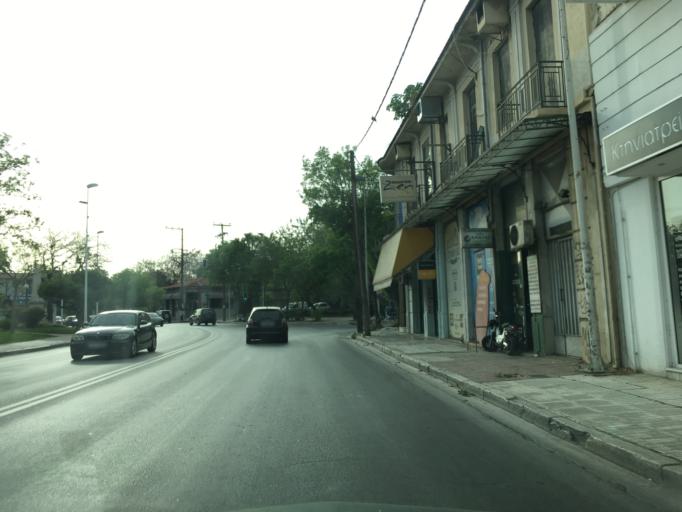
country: GR
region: Thessaly
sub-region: Nomos Magnisias
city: Nea Ionia
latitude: 39.3625
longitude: 22.9371
